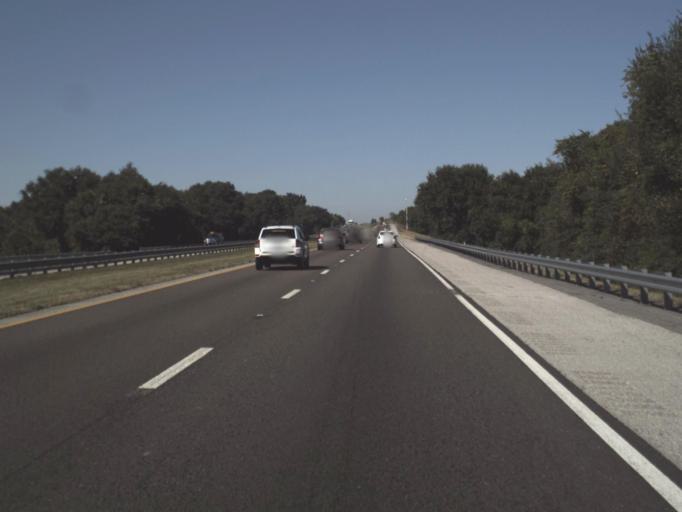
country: US
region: Florida
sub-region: Lake County
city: Minneola
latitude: 28.6211
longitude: -81.7489
